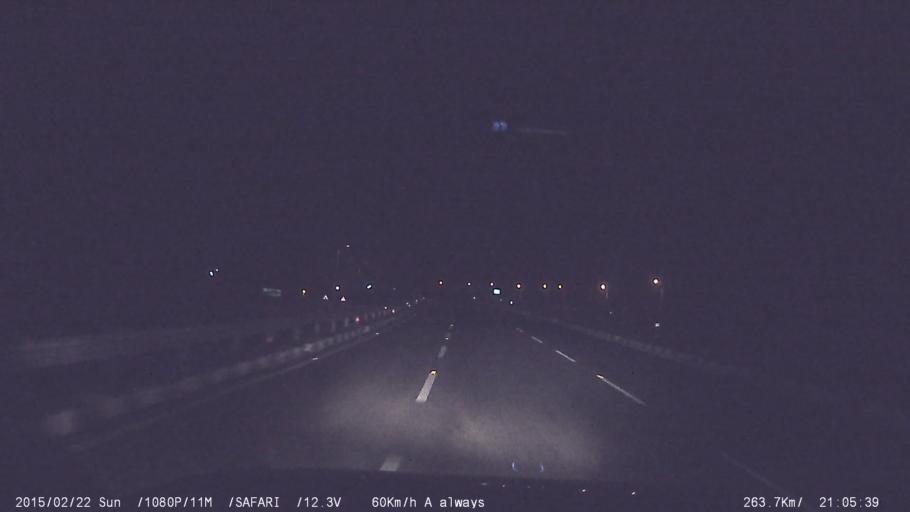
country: IN
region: Tamil Nadu
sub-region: Karur
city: Pallappatti
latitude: 10.7022
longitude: 77.9334
